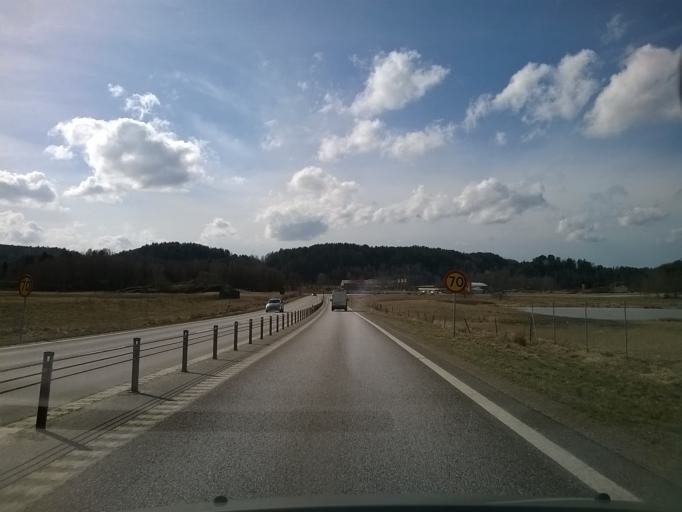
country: SE
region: Vaestra Goetaland
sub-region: Orust
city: Henan
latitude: 58.3446
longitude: 11.6989
